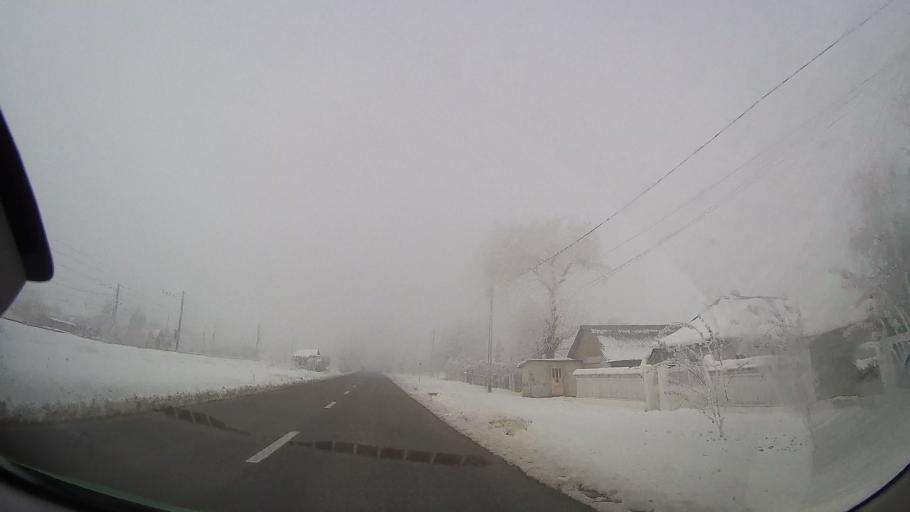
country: RO
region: Iasi
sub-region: Comuna Mircesti
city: Mircesti
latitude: 47.0886
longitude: 26.8242
